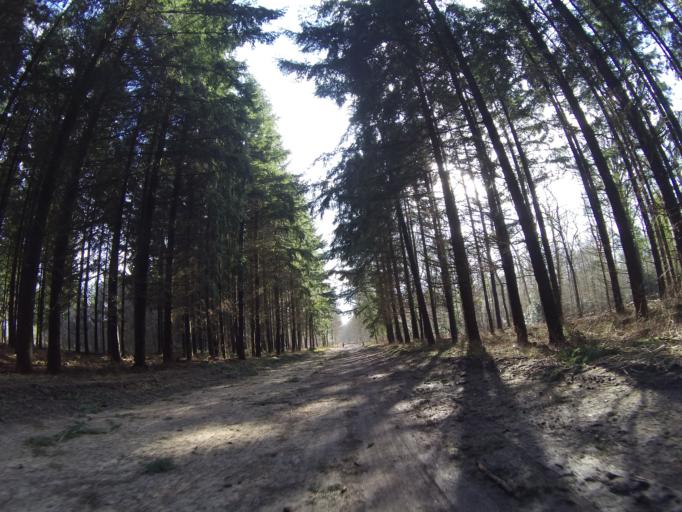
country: NL
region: Utrecht
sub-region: Gemeente Soest
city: Soest
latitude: 52.1363
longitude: 5.2570
